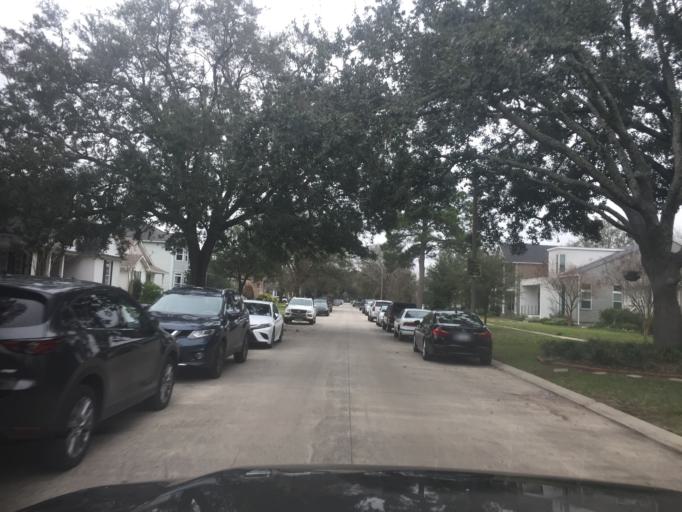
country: US
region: Louisiana
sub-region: Orleans Parish
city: New Orleans
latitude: 29.9956
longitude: -90.1038
